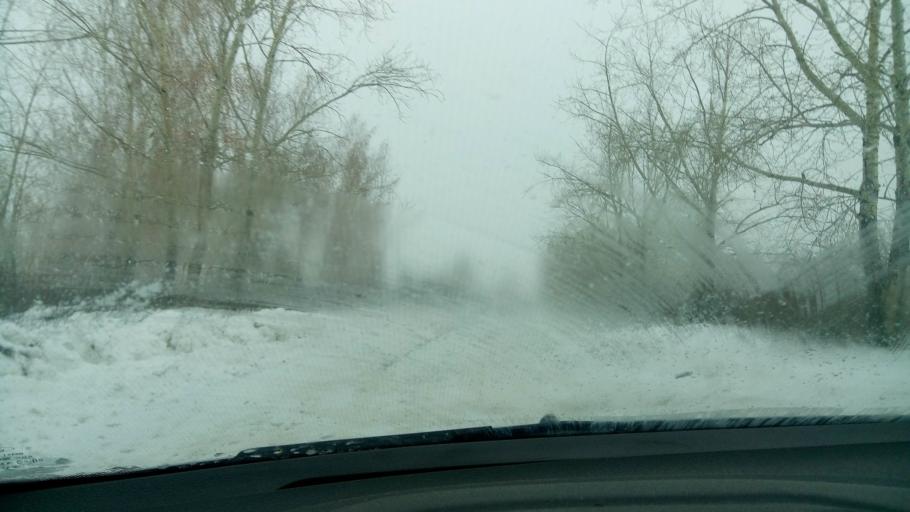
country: RU
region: Sverdlovsk
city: Bogdanovich
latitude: 56.7997
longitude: 62.0496
